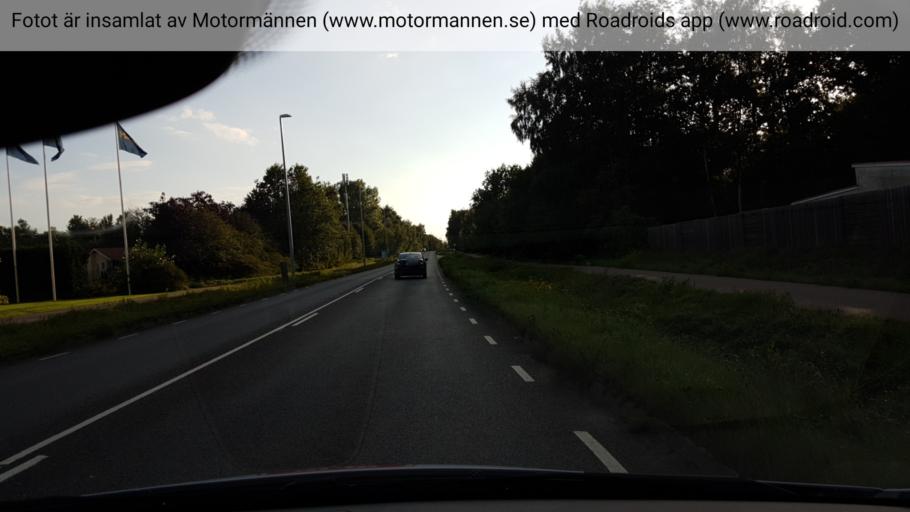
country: SE
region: Halland
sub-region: Halmstads Kommun
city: Mjallby
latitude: 56.6592
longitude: 12.8053
